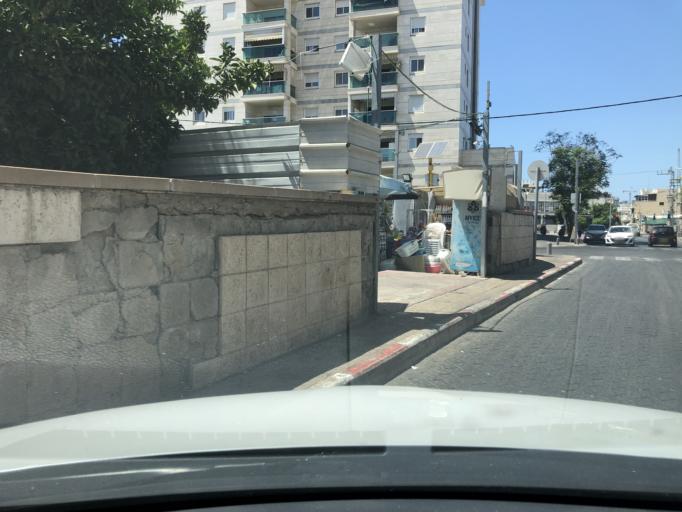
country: IL
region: Tel Aviv
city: Azor
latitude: 32.0463
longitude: 34.7918
